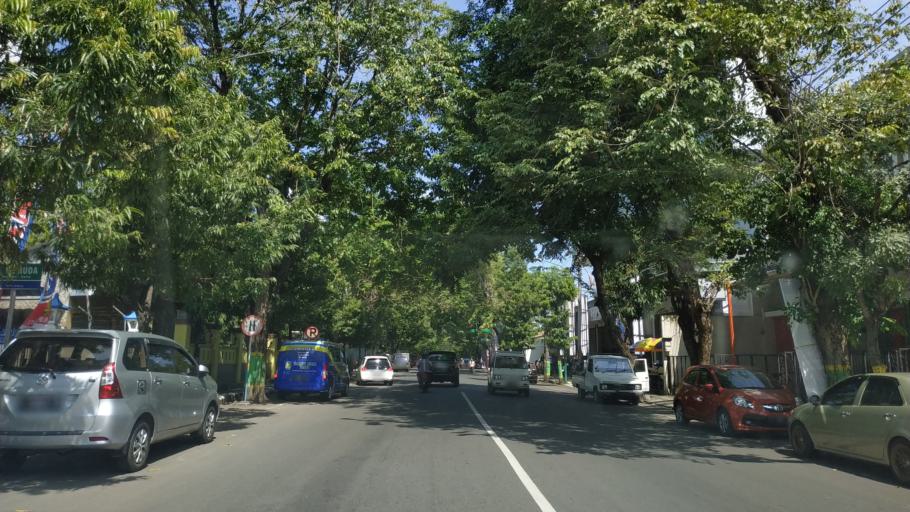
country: ID
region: Central Java
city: Baran
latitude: -6.7529
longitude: 111.0508
